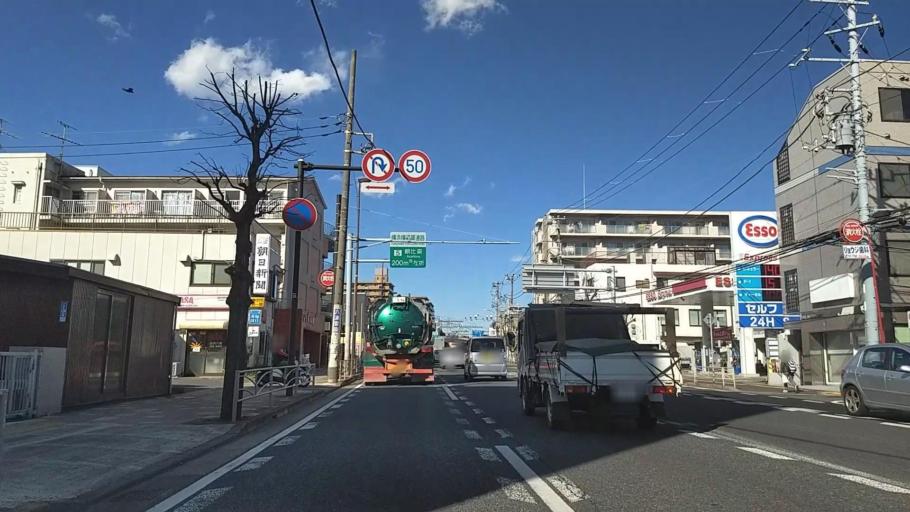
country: JP
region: Kanagawa
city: Zushi
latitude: 35.3259
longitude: 139.6201
